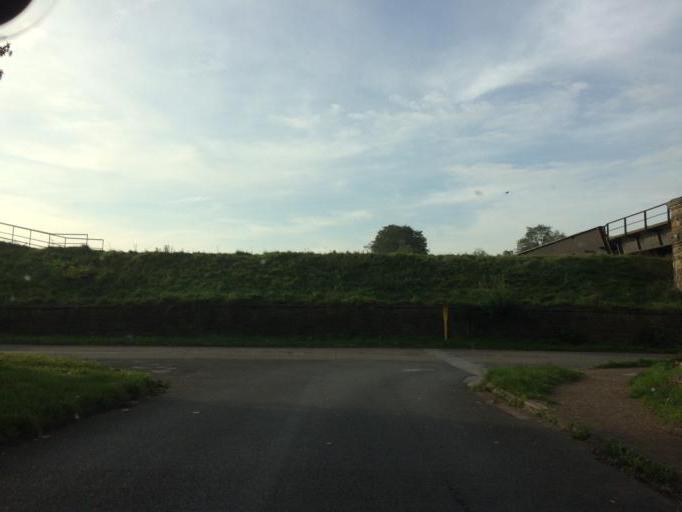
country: DE
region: North Rhine-Westphalia
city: Dorsten
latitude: 51.6673
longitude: 6.9726
